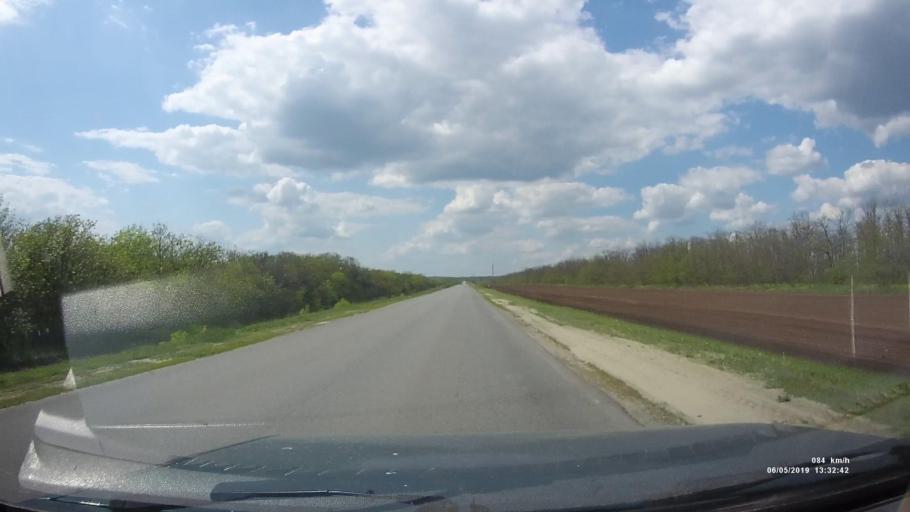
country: RU
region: Rostov
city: Ust'-Donetskiy
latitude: 47.6854
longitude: 40.7912
